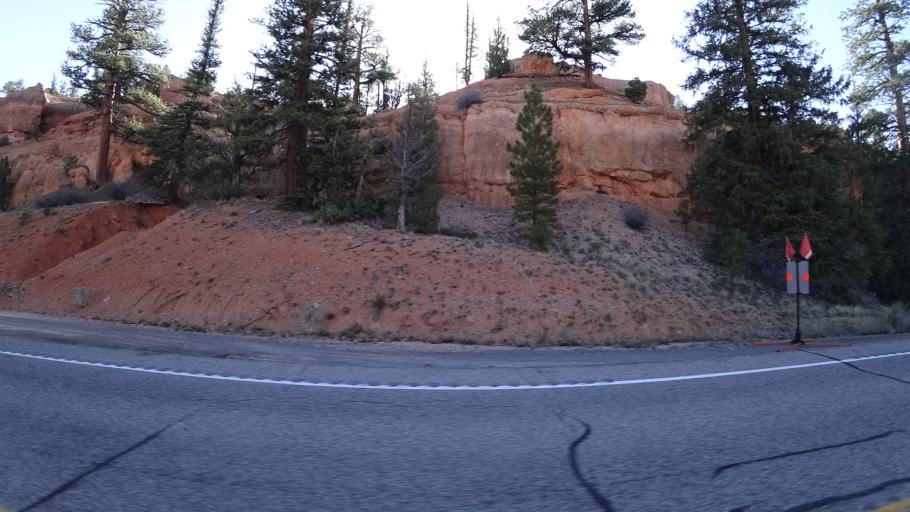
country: US
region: Utah
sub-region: Garfield County
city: Panguitch
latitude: 37.7434
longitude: -112.3008
